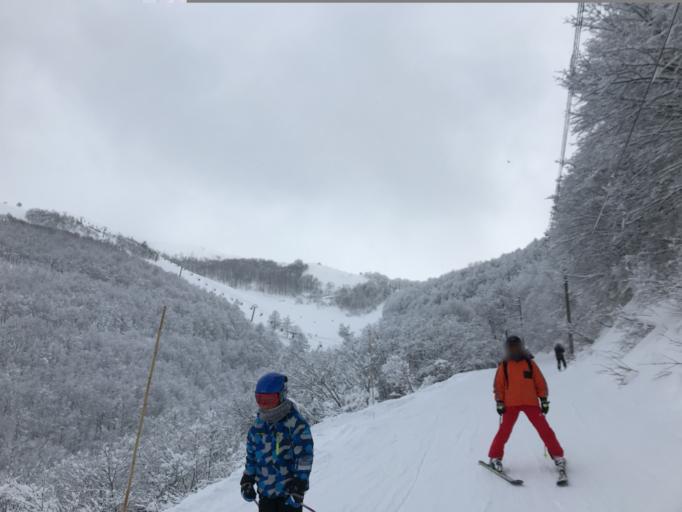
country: JP
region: Nagano
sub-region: Kitaazumi Gun
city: Hakuba
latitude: 36.7081
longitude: 137.8199
